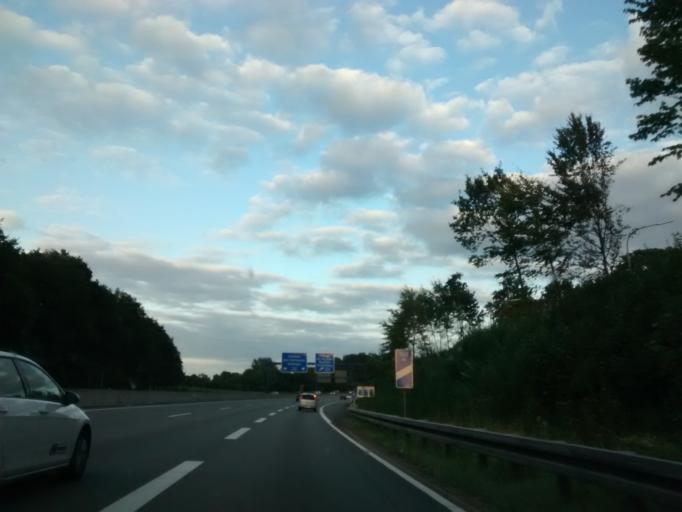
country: DE
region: Lower Saxony
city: Osnabrueck
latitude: 52.2465
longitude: 8.0748
